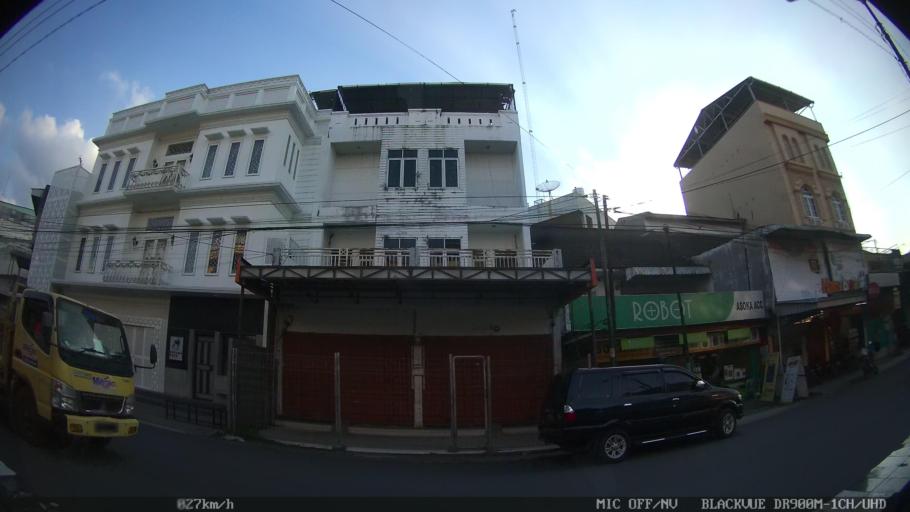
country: ID
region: North Sumatra
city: Medan
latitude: 3.5963
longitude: 98.6653
